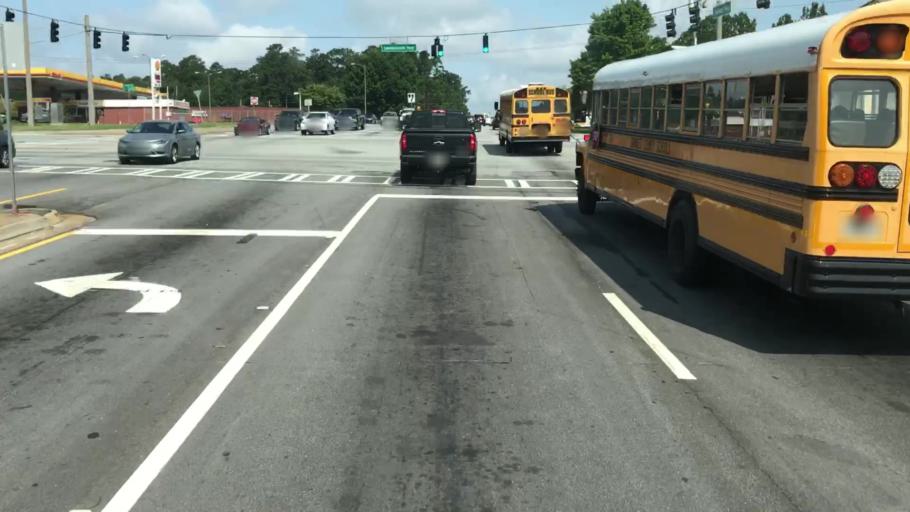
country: US
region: Georgia
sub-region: Gwinnett County
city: Lawrenceville
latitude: 33.9382
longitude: -84.0336
